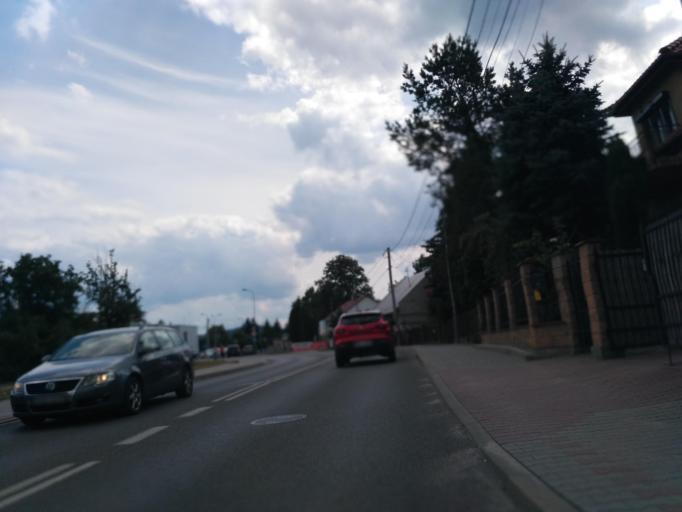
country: PL
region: Subcarpathian Voivodeship
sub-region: Powiat debicki
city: Debica
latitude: 50.0463
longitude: 21.4096
